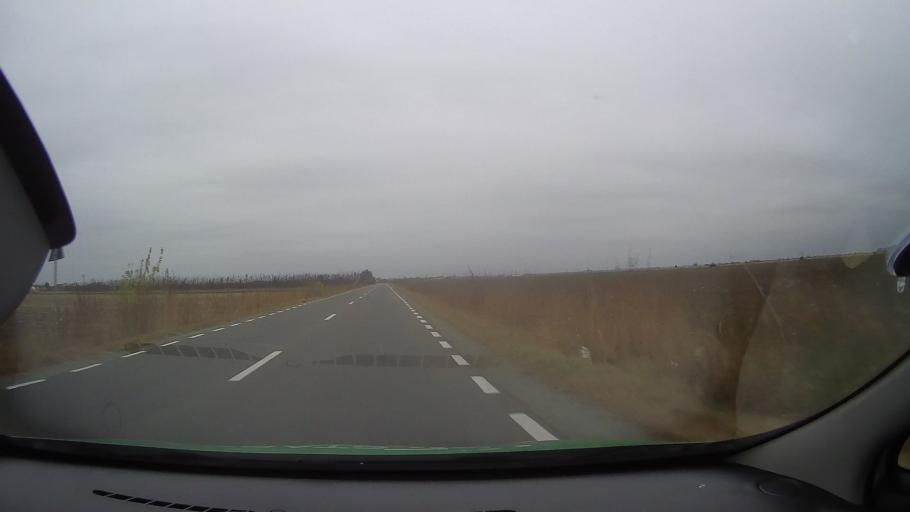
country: RO
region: Ialomita
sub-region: Comuna Slobozia
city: Slobozia
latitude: 44.6147
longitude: 27.3864
